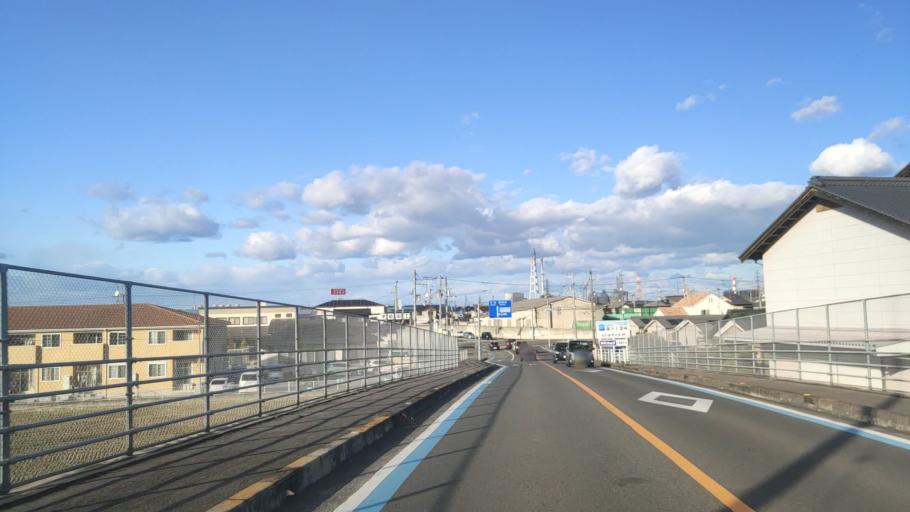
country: JP
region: Ehime
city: Saijo
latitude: 33.9140
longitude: 133.1620
